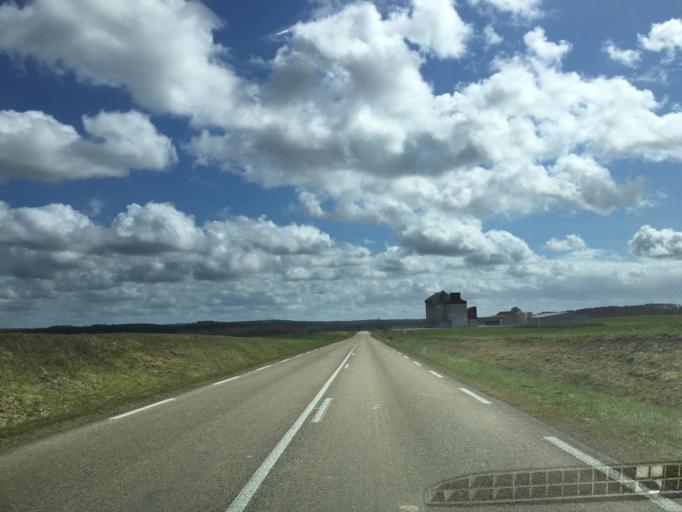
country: FR
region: Bourgogne
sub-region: Departement de l'Yonne
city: Aillant-sur-Tholon
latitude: 47.8530
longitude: 3.3767
